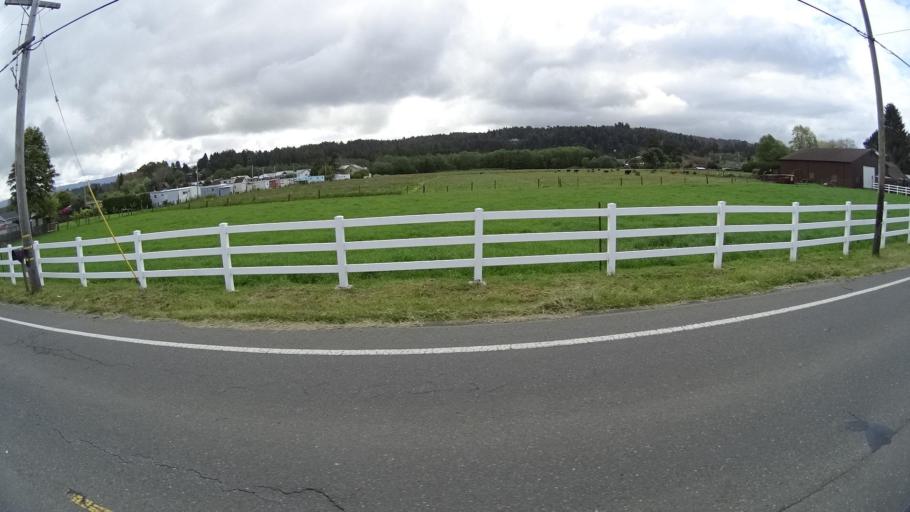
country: US
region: California
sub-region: Humboldt County
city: Arcata
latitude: 40.8878
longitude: -124.0884
